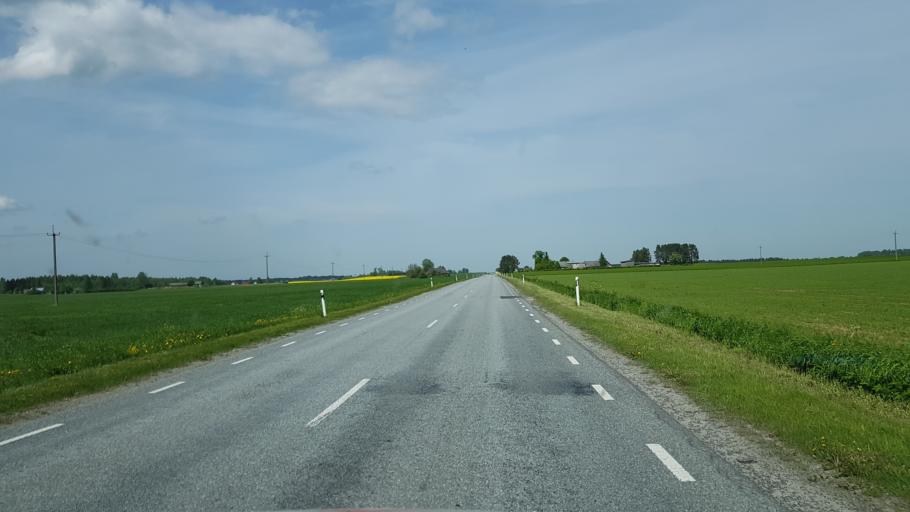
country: EE
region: Laeaene-Virumaa
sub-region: Tapa vald
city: Tapa
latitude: 59.2884
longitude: 25.9974
